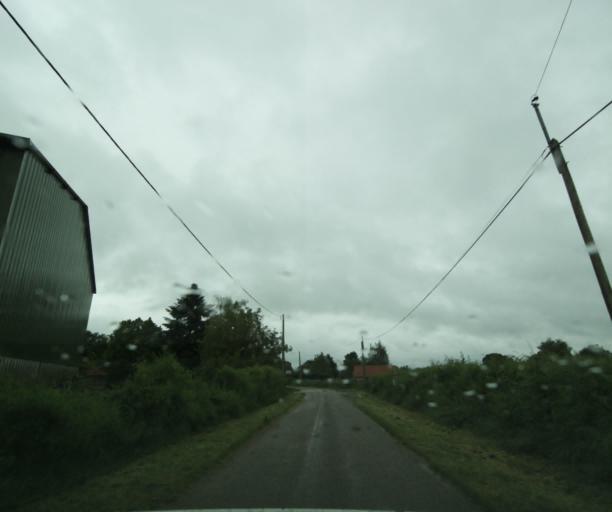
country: FR
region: Bourgogne
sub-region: Departement de Saone-et-Loire
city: Charolles
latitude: 46.4770
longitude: 4.2958
